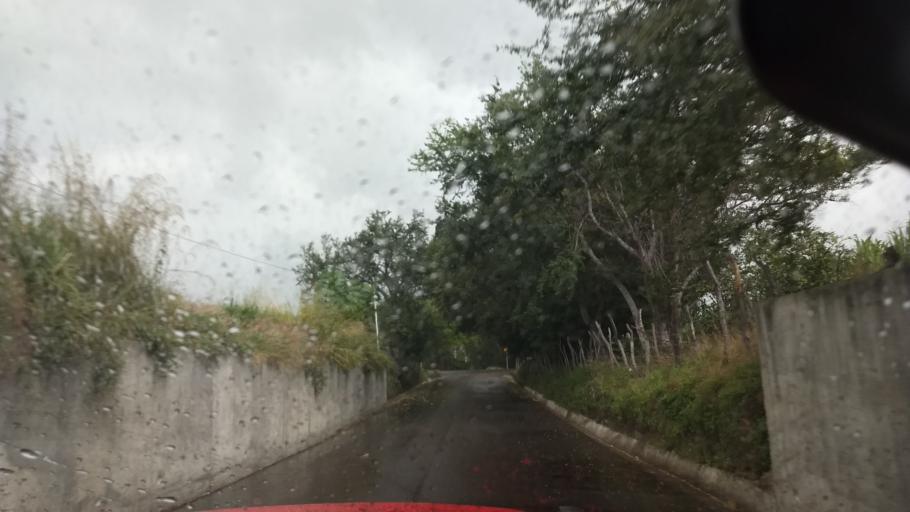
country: MX
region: Jalisco
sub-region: Tonila
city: San Marcos
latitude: 19.4406
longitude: -103.4909
